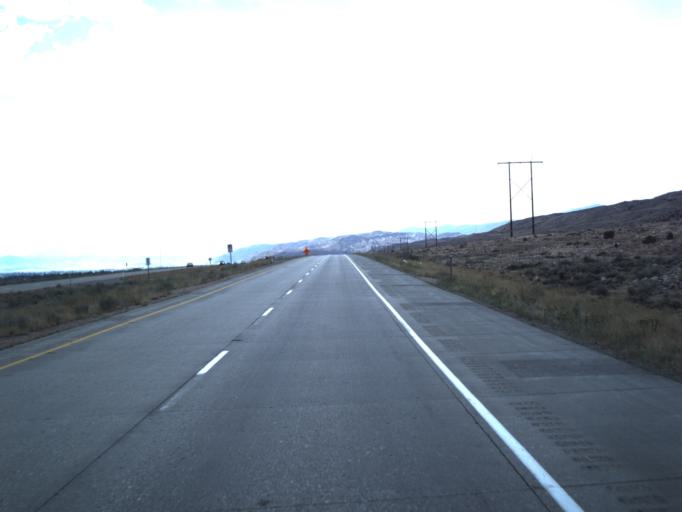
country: US
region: Utah
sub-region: Sevier County
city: Richfield
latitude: 38.8202
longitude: -112.0471
